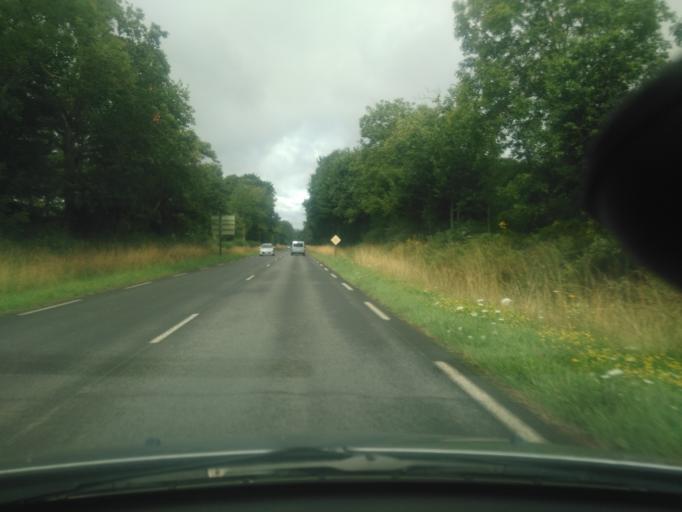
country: FR
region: Brittany
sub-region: Departement des Cotes-d'Armor
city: Les Champs-Geraux
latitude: 48.4448
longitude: -1.9770
